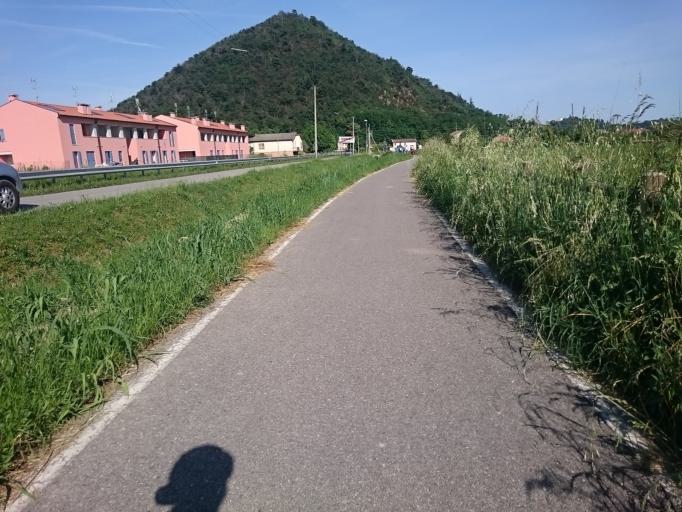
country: IT
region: Veneto
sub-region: Provincia di Padova
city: Torreglia
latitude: 45.3533
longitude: 11.7432
